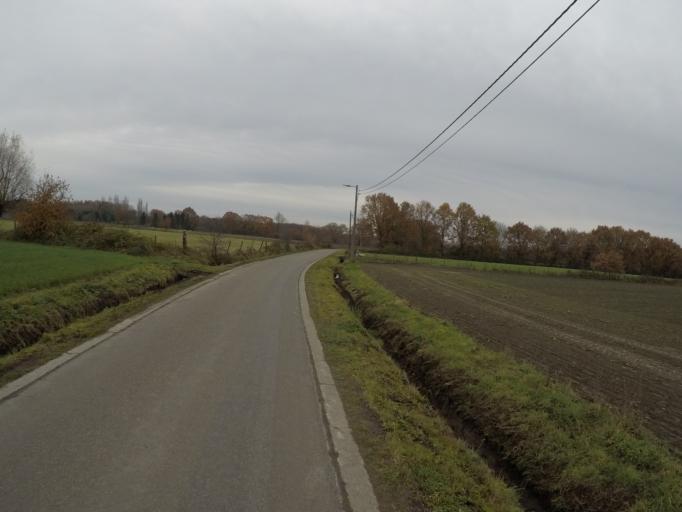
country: BE
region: Flanders
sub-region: Provincie Antwerpen
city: Heist-op-den-Berg
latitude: 51.0972
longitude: 4.7238
